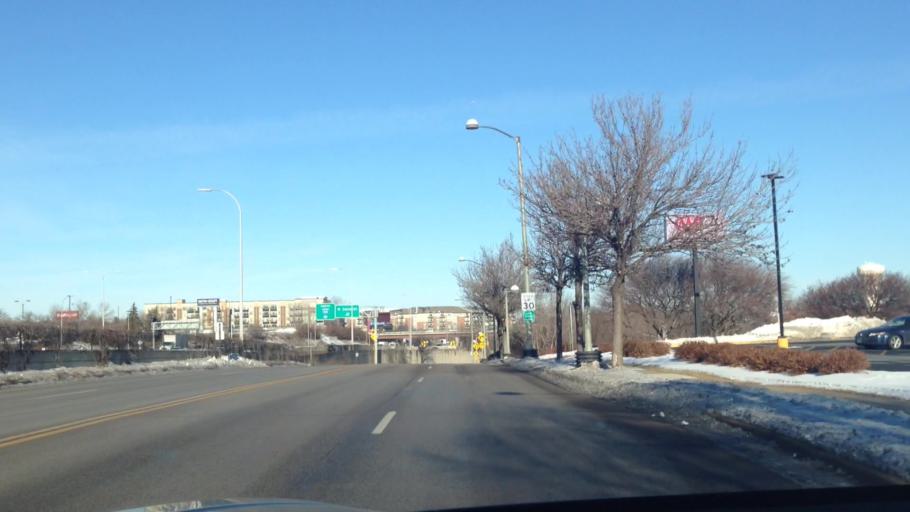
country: US
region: Minnesota
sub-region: Hennepin County
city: Saint Louis Park
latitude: 44.9334
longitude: -93.3494
